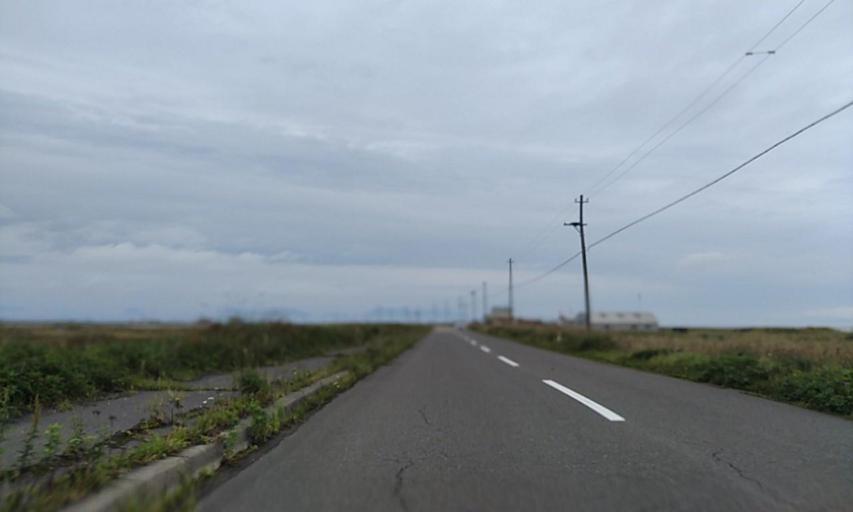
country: JP
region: Hokkaido
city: Shibetsu
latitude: 43.5812
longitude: 145.3428
